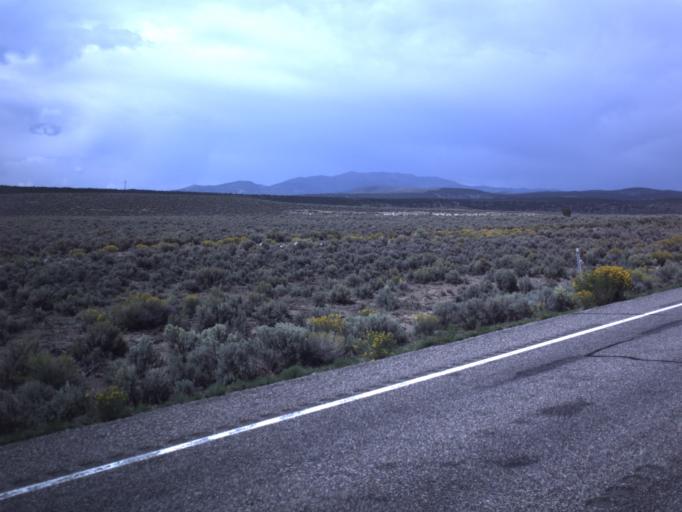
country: US
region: Utah
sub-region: Garfield County
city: Panguitch
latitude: 37.9868
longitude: -112.3959
